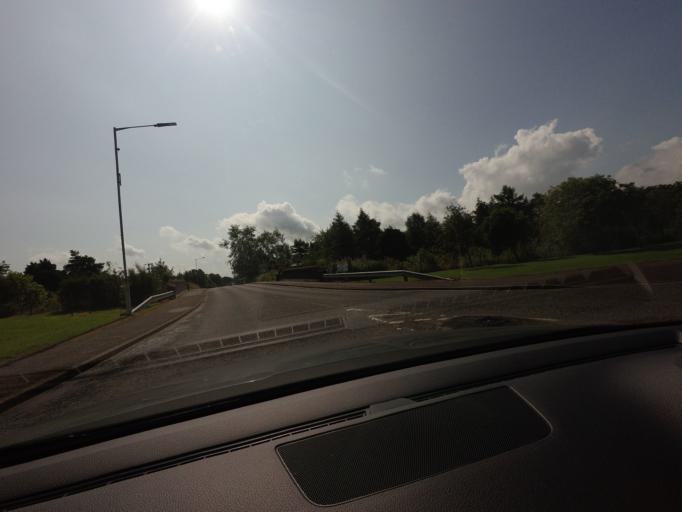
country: GB
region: Scotland
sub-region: Highland
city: Alness
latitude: 57.6925
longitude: -4.2706
